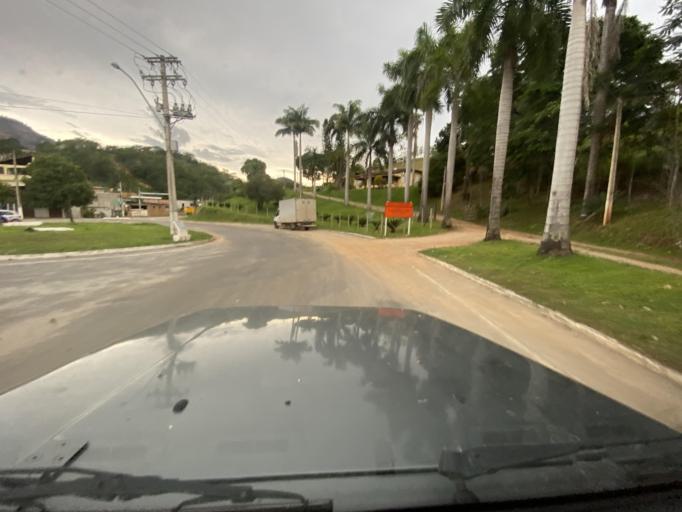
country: BR
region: Espirito Santo
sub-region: Jeronimo Monteiro
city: Jeronimo Monteiro
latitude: -20.8006
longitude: -41.3709
